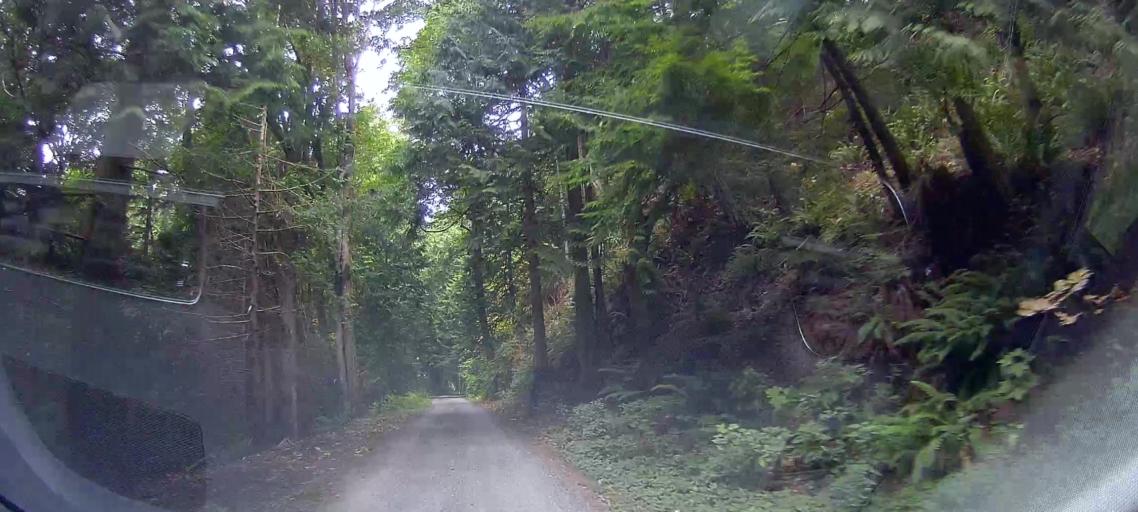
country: US
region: Washington
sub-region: Whatcom County
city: Geneva
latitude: 48.6183
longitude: -122.4375
